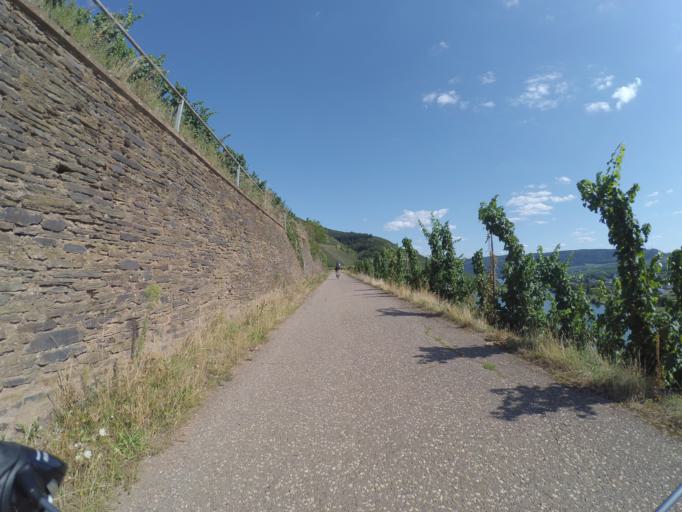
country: DE
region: Rheinland-Pfalz
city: Schweich
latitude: 49.8161
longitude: 6.7652
